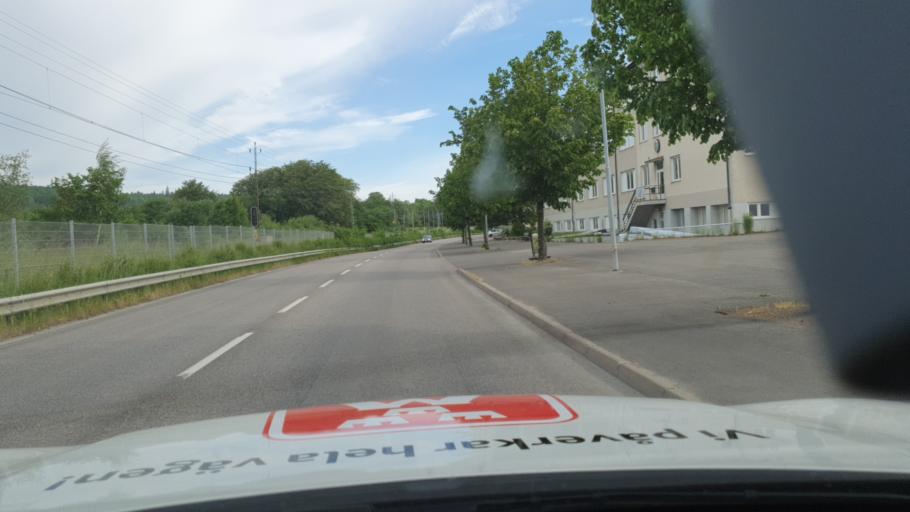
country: SE
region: Vaestra Goetaland
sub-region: Falkopings Kommun
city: Falkoeping
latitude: 58.1680
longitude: 13.5449
